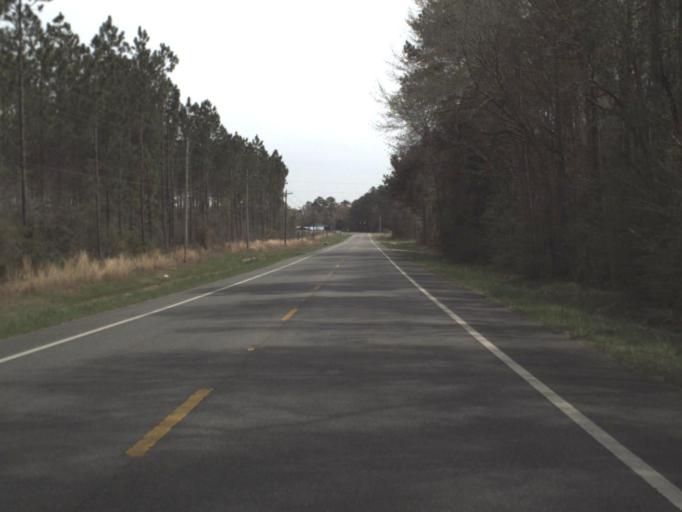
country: US
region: Alabama
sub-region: Geneva County
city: Geneva
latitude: 30.9537
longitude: -85.8837
